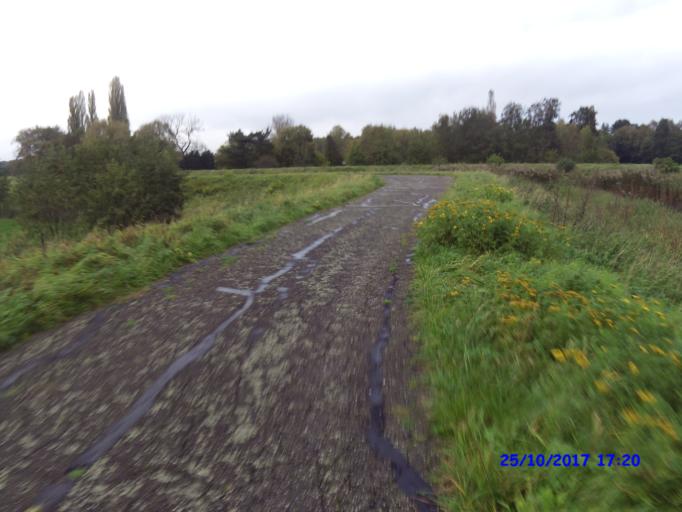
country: BE
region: Flanders
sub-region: Provincie Antwerpen
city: Lier
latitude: 51.1362
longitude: 4.6062
